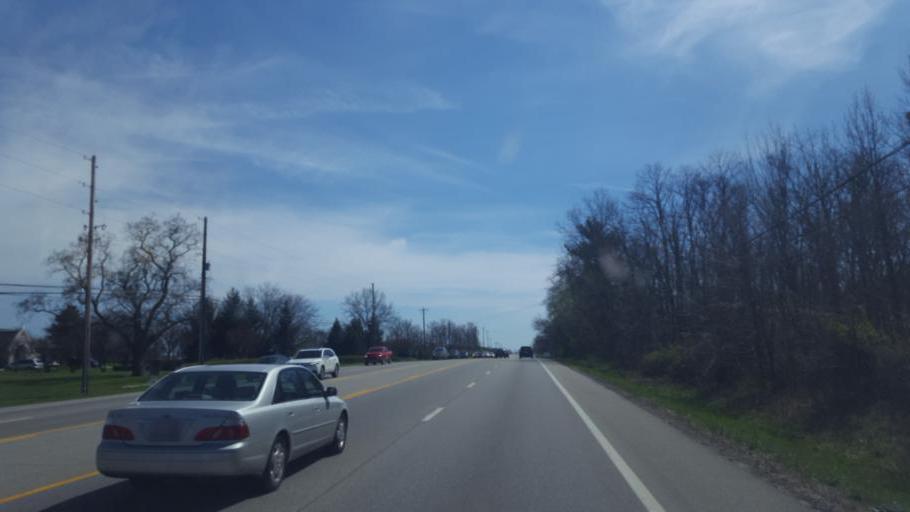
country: US
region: Ohio
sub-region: Delaware County
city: Lewis Center
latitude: 40.1504
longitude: -83.0181
